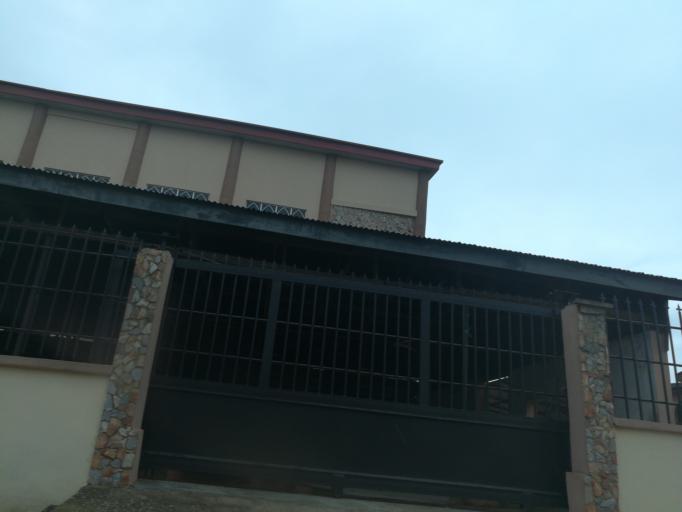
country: NG
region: Lagos
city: Oshodi
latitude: 6.5692
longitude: 3.3404
